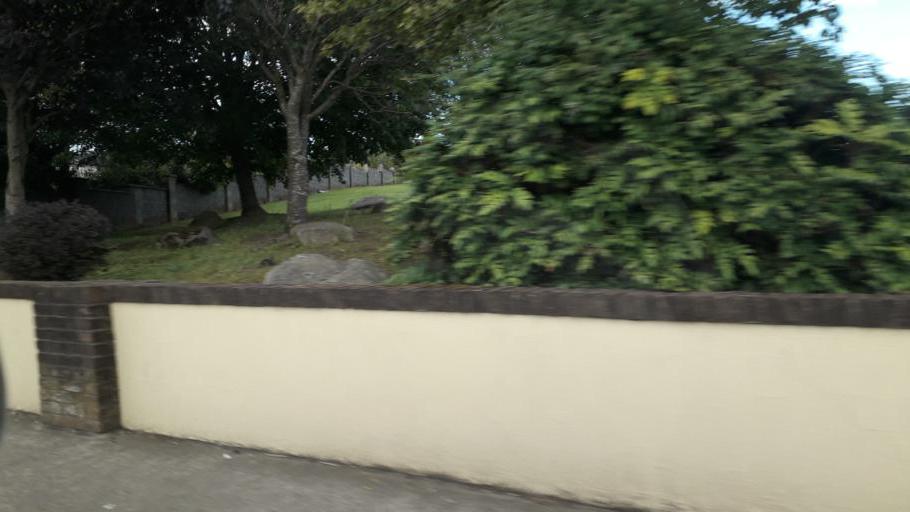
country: IE
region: Leinster
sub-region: Loch Garman
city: Gorey
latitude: 52.6779
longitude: -6.2859
